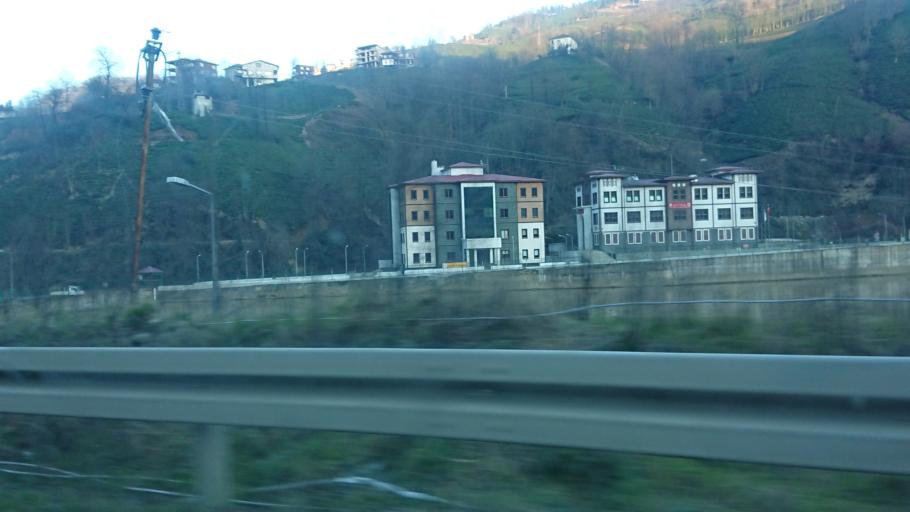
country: TR
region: Rize
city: Gundogdu
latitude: 41.0214
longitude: 40.5759
